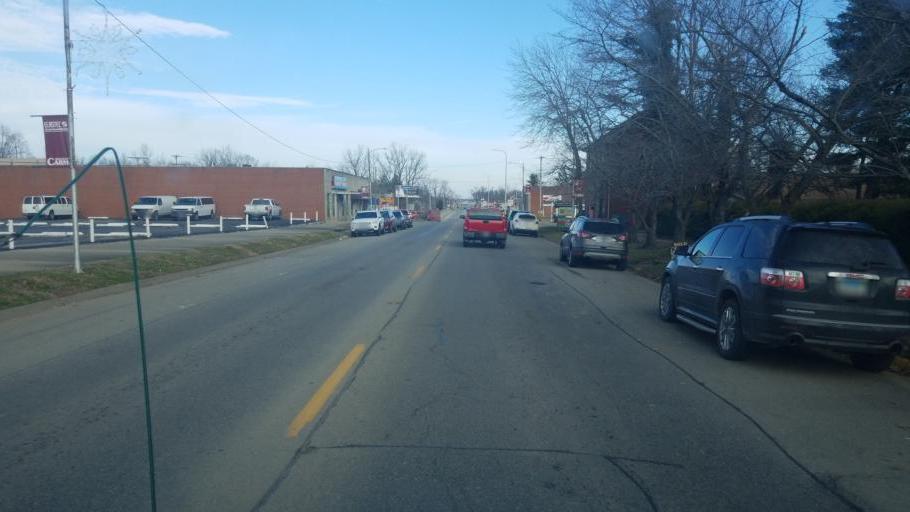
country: US
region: Illinois
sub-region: White County
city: Carmi
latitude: 38.0909
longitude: -88.1586
